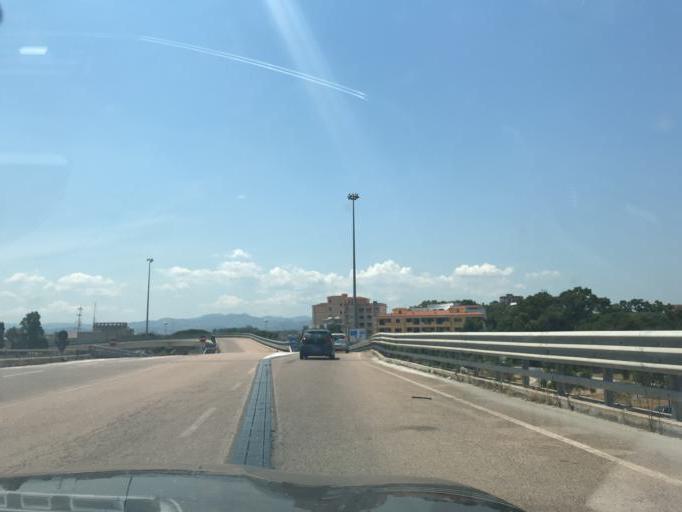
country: IT
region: Sardinia
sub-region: Provincia di Olbia-Tempio
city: Olbia
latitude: 40.9273
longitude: 9.5076
